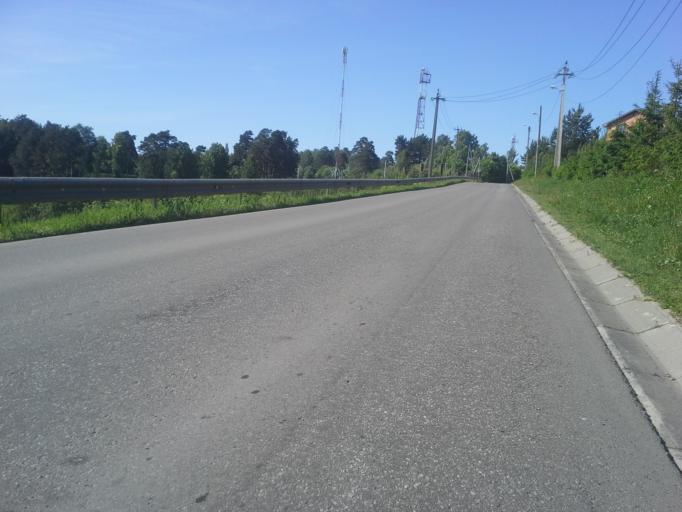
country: RU
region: Moskovskaya
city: Vatutinki
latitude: 55.4498
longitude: 37.3986
